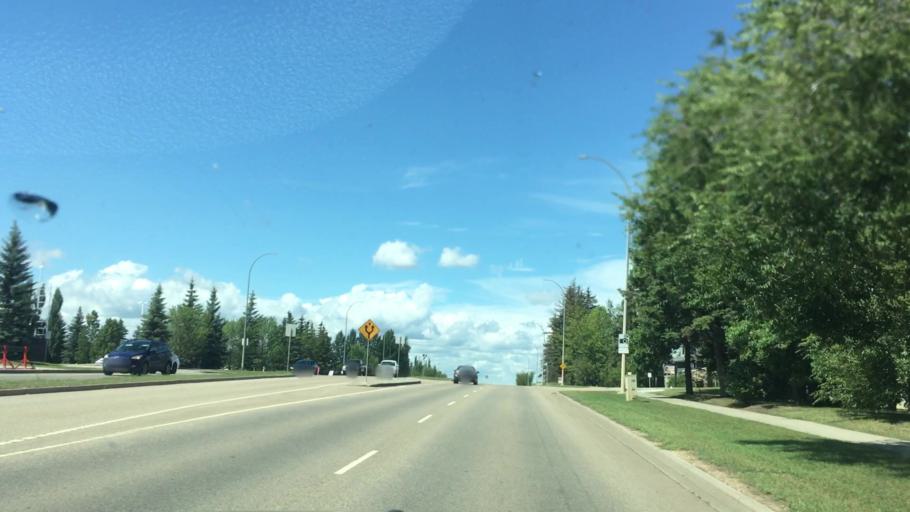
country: CA
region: Alberta
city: Beaumont
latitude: 53.4250
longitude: -113.5005
